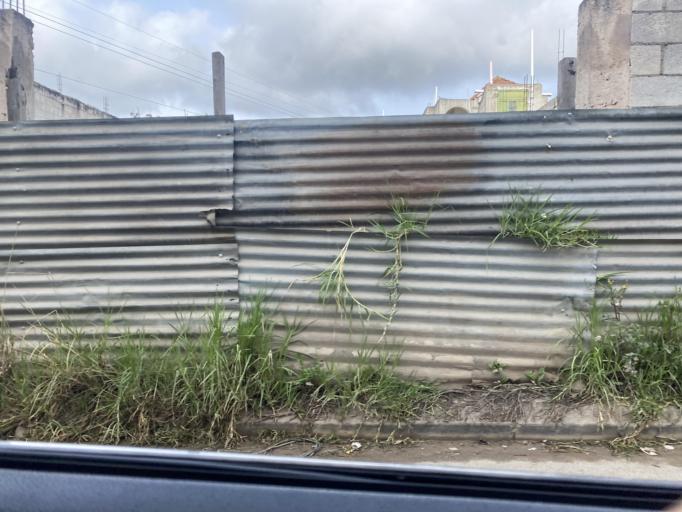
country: GT
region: Quetzaltenango
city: Quetzaltenango
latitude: 14.8574
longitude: -91.5193
